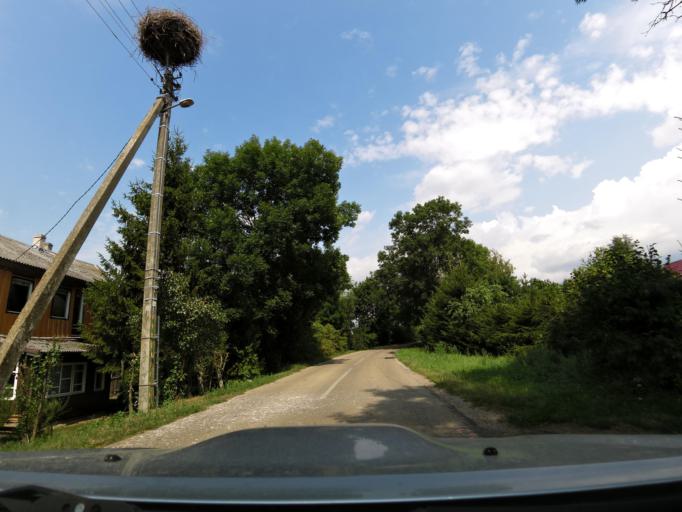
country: LT
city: Rusne
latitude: 55.3058
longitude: 21.3776
